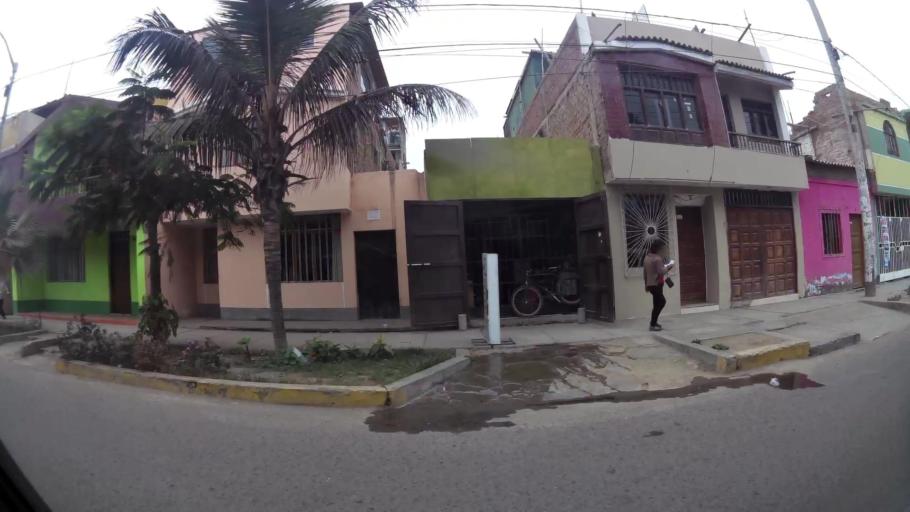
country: PE
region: La Libertad
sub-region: Provincia de Trujillo
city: Buenos Aires
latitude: -8.1364
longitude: -79.0432
